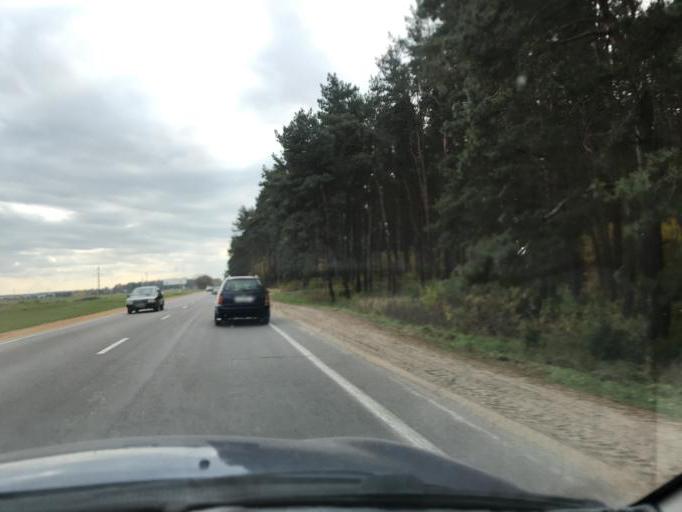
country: BY
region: Grodnenskaya
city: Lida
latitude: 53.8815
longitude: 25.2560
